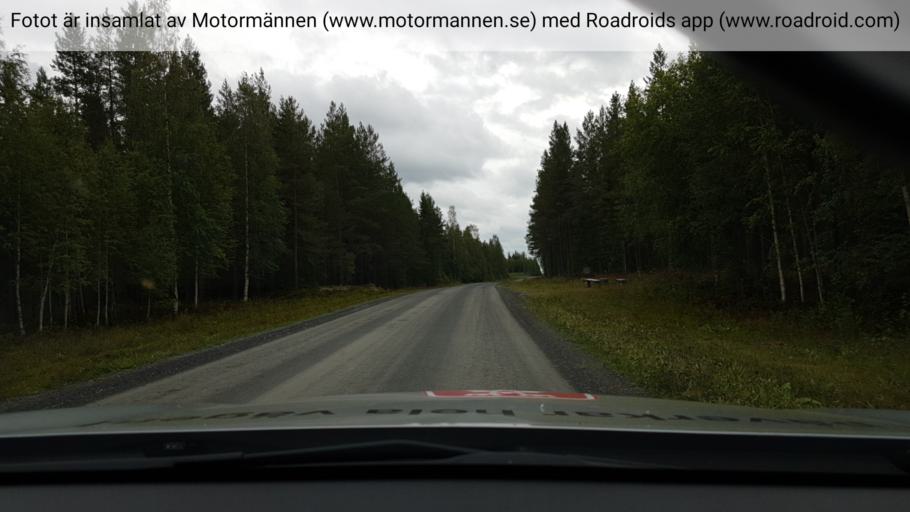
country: SE
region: Vaesterbotten
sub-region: Skelleftea Kommun
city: Forsbacka
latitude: 64.8049
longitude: 20.5013
